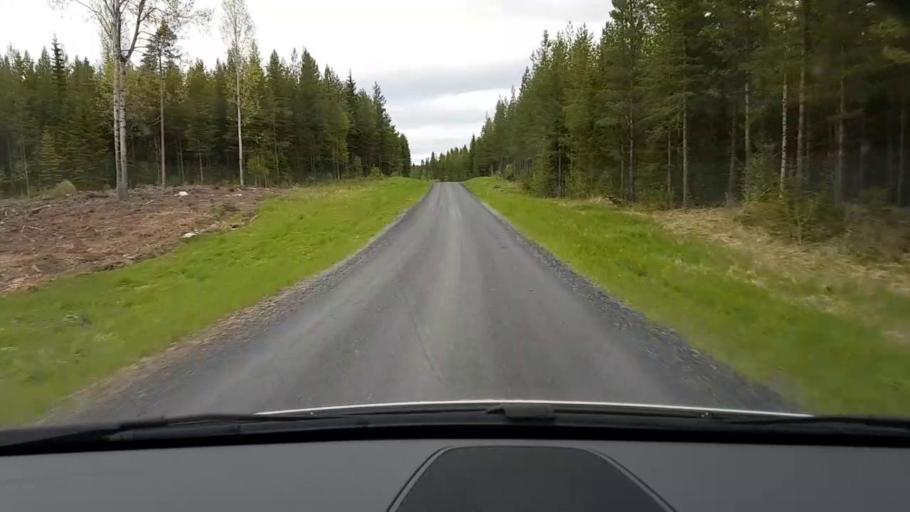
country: SE
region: Jaemtland
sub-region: Krokoms Kommun
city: Krokom
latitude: 63.3023
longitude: 14.3973
